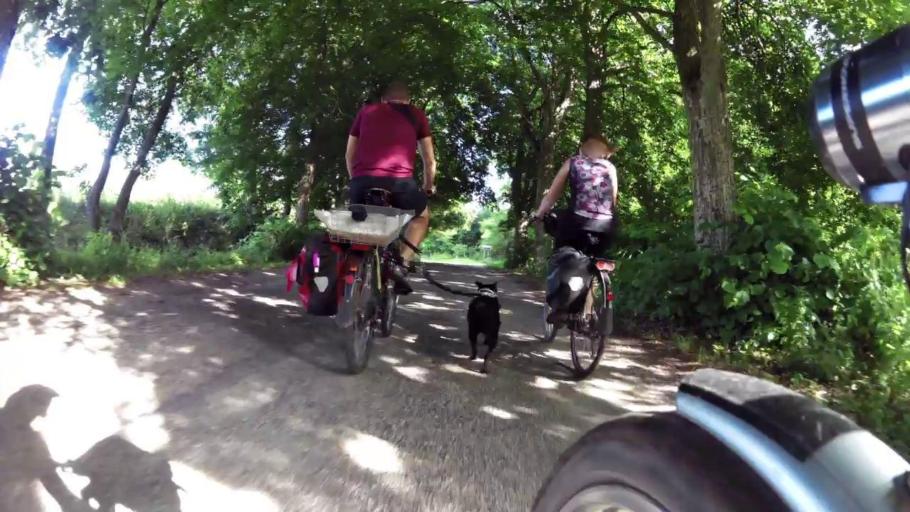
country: PL
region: West Pomeranian Voivodeship
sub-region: Powiat lobeski
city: Radowo Male
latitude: 53.5821
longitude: 15.4590
